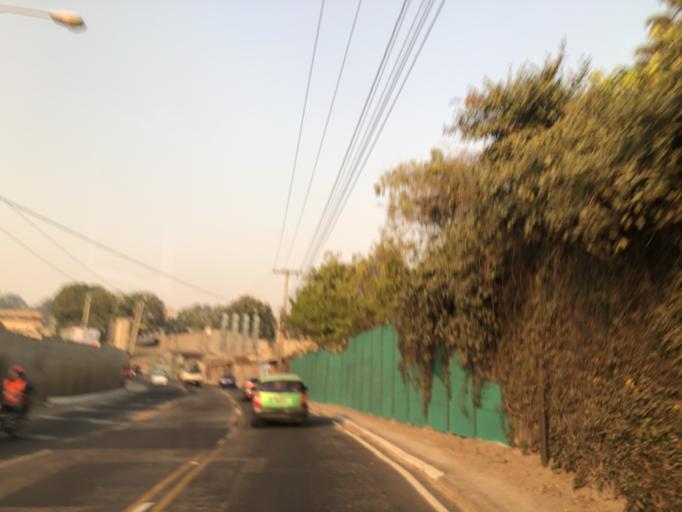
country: GT
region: Guatemala
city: Santa Catarina Pinula
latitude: 14.5617
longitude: -90.5287
